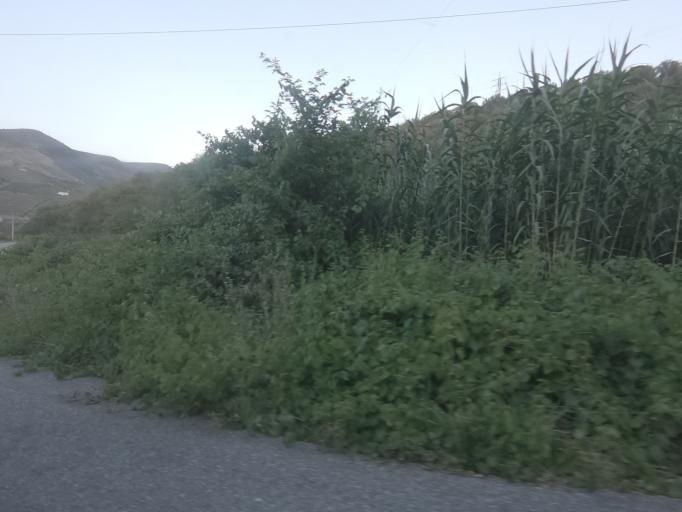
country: PT
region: Vila Real
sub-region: Peso da Regua
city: Peso da Regua
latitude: 41.1434
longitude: -7.7422
